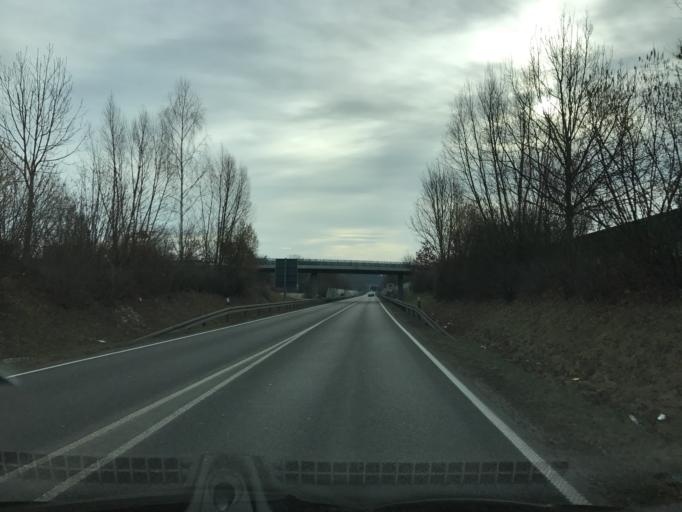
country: DE
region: Baden-Wuerttemberg
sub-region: Tuebingen Region
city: Eriskirch
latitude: 47.6327
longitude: 9.5302
